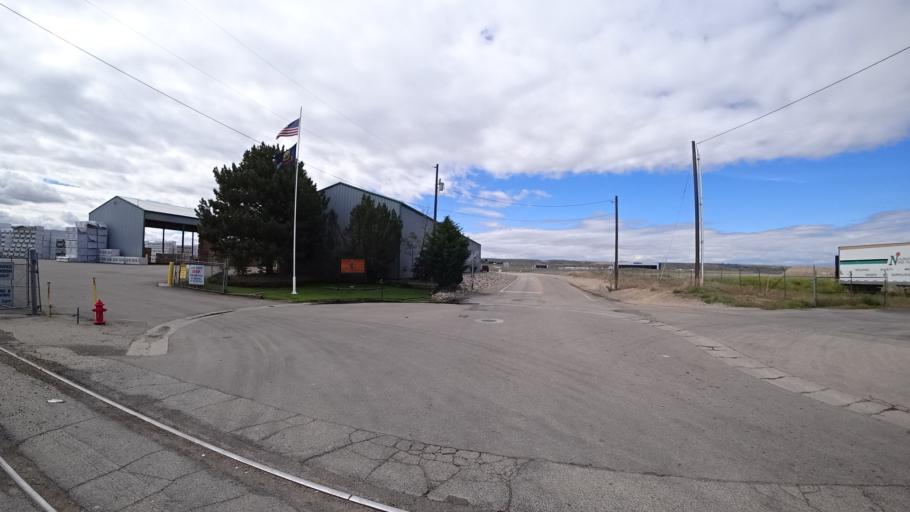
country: US
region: Idaho
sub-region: Ada County
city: Boise
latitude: 43.5590
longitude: -116.1933
